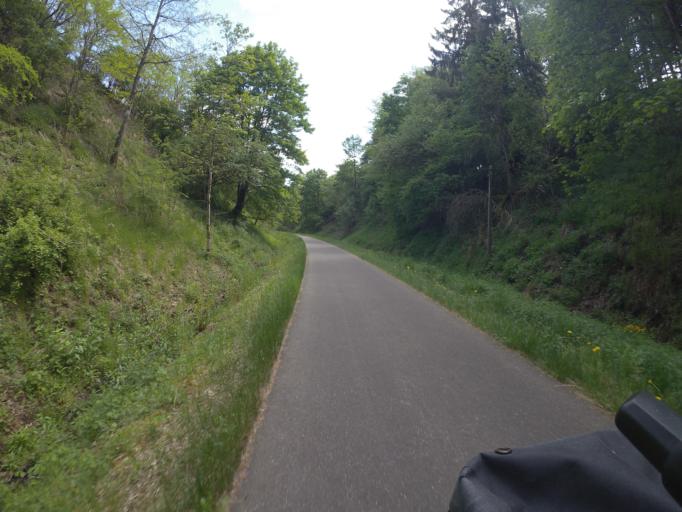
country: DE
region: Rheinland-Pfalz
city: Scheid
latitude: 50.3508
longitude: 6.4005
